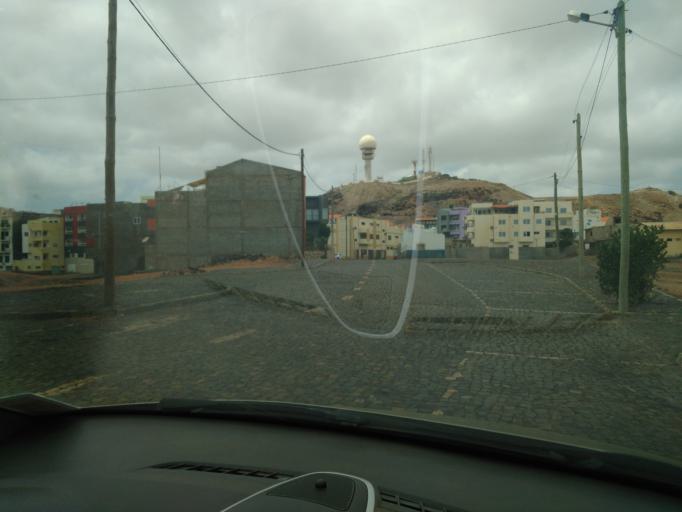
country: CV
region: Sal
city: Espargos
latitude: 16.7539
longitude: -22.9409
